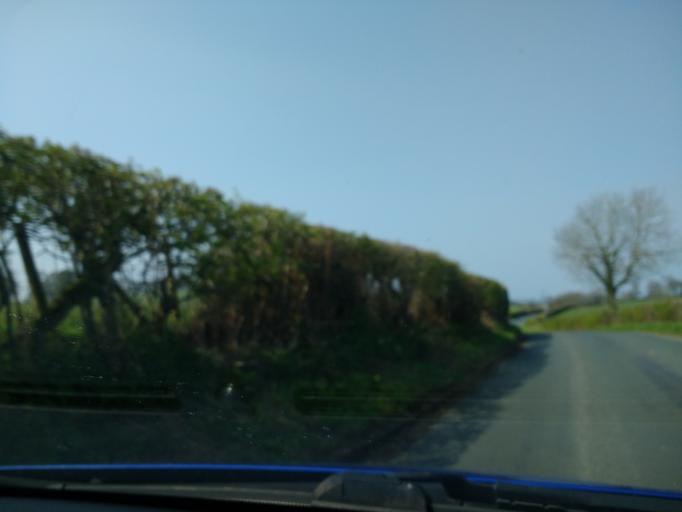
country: GB
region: England
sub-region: Lancashire
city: Bolton le Sands
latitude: 54.0865
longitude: -2.7968
